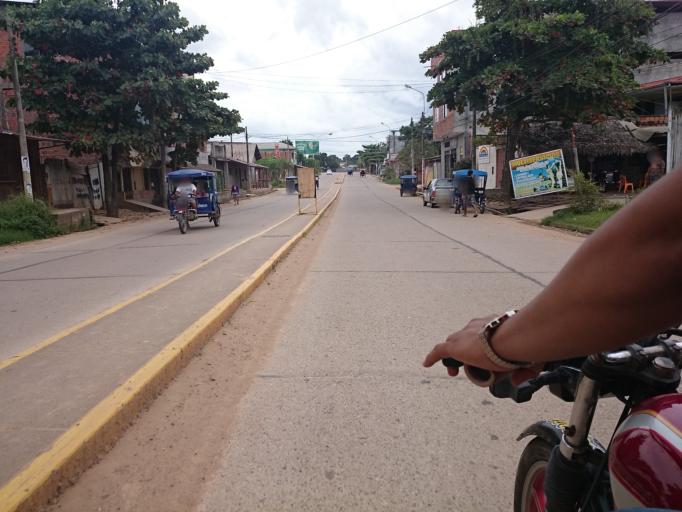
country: PE
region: Ucayali
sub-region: Provincia de Coronel Portillo
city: Puerto Callao
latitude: -8.3677
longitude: -74.5666
